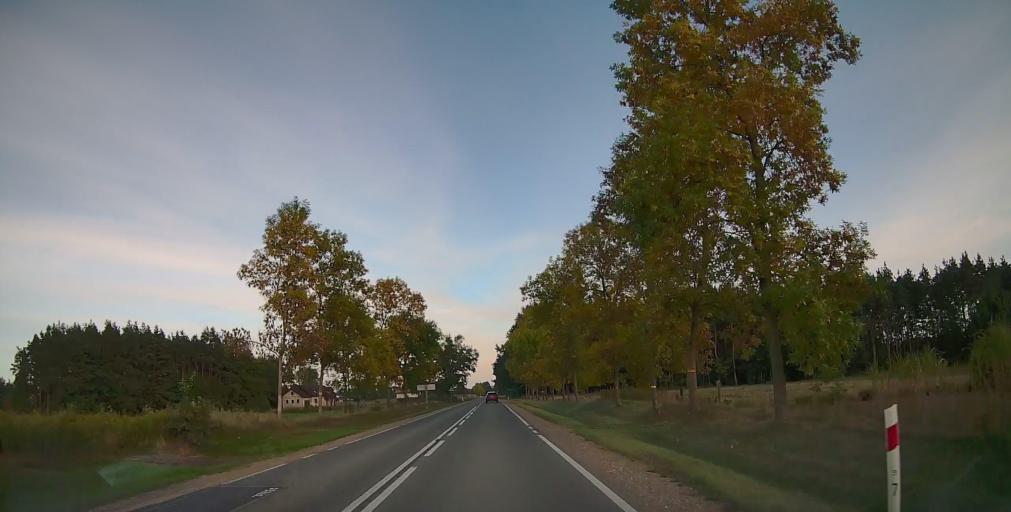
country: PL
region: Masovian Voivodeship
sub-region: Powiat garwolinski
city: Wilga
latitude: 51.7968
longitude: 21.3451
